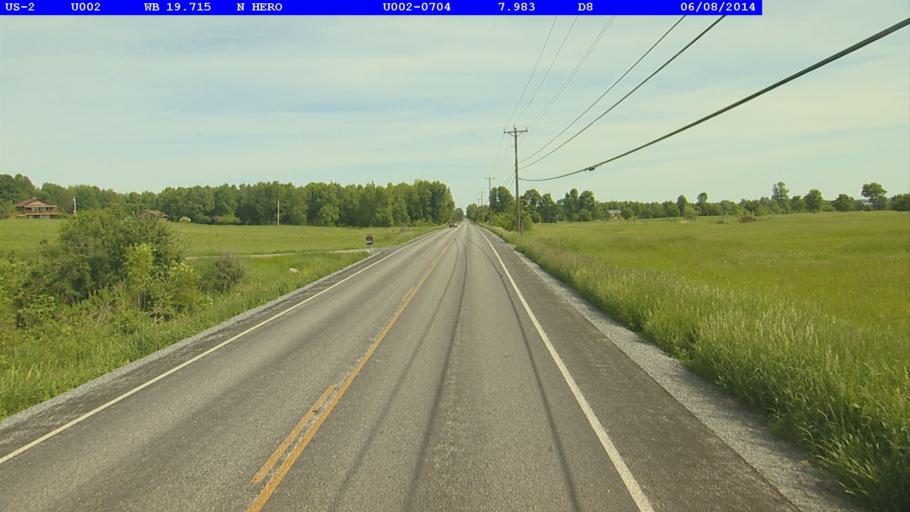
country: US
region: Vermont
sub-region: Grand Isle County
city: North Hero
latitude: 44.7848
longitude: -73.2932
